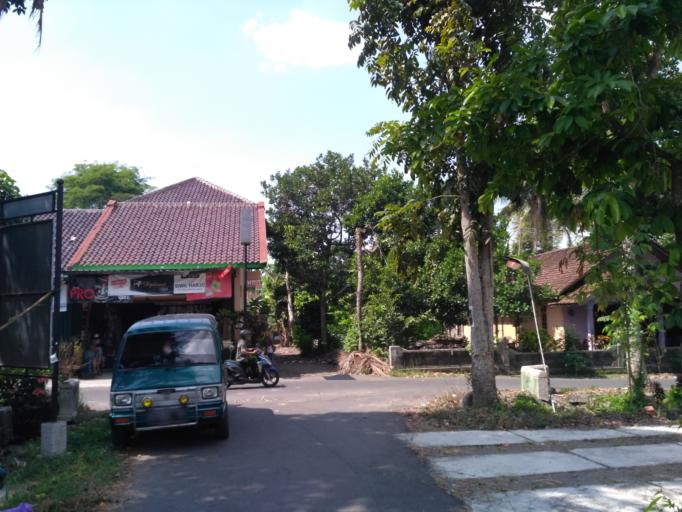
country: ID
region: Daerah Istimewa Yogyakarta
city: Depok
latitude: -7.7111
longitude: 110.4239
